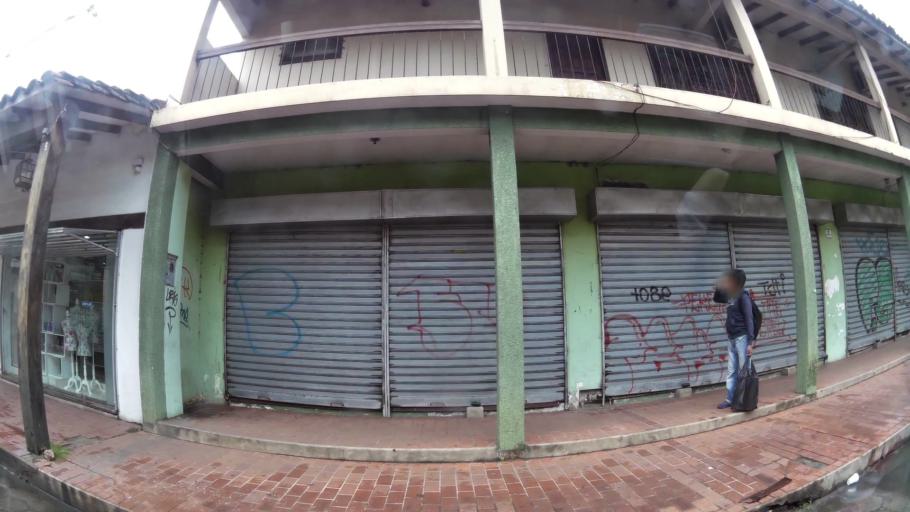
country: BO
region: Santa Cruz
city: Santa Cruz de la Sierra
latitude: -17.7865
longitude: -63.1786
